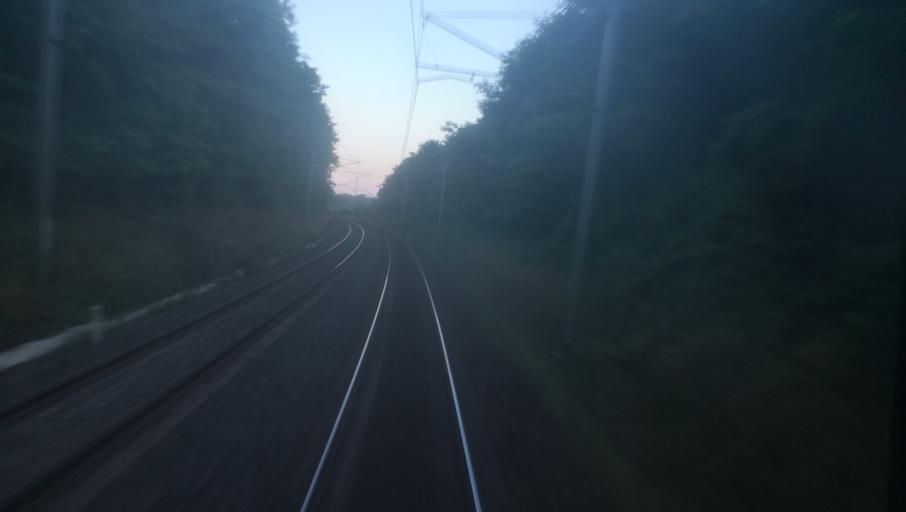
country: FR
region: Centre
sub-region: Departement du Cher
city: Saint-Satur
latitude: 47.3445
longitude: 2.8805
